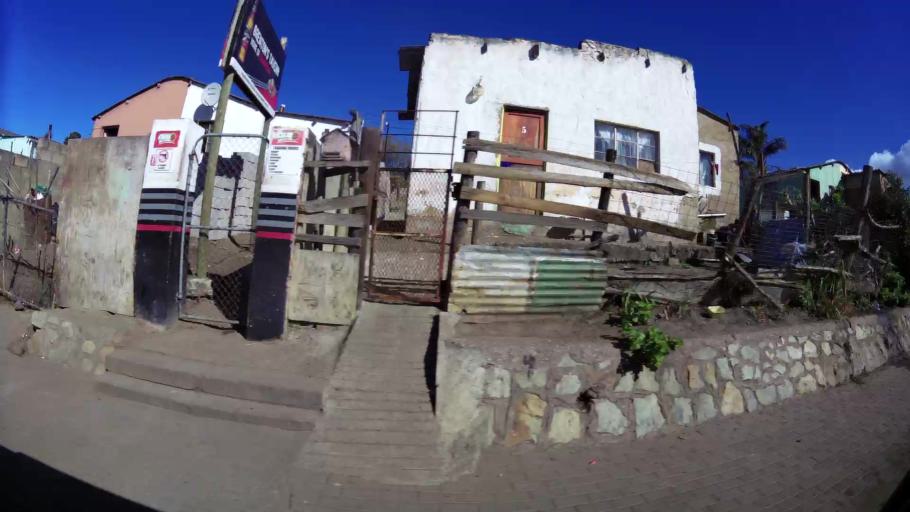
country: ZA
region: Western Cape
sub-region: Eden District Municipality
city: George
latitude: -33.9402
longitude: 22.4094
